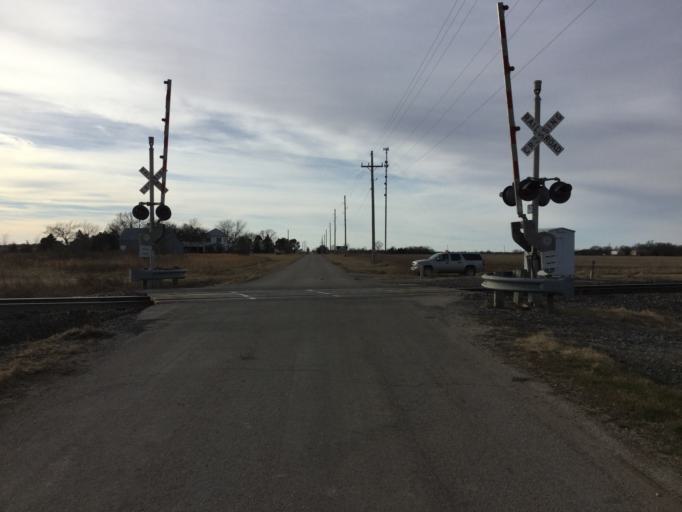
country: US
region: Kansas
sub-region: Allen County
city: Iola
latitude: 37.9071
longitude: -95.1625
